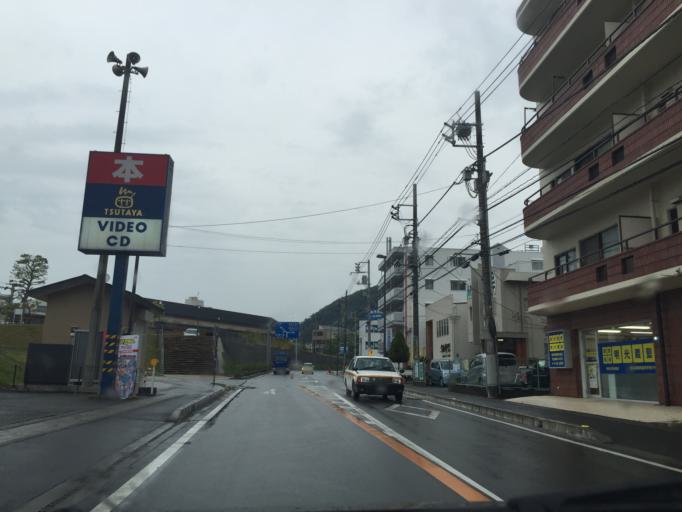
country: JP
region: Shizuoka
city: Ito
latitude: 34.9805
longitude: 138.9512
